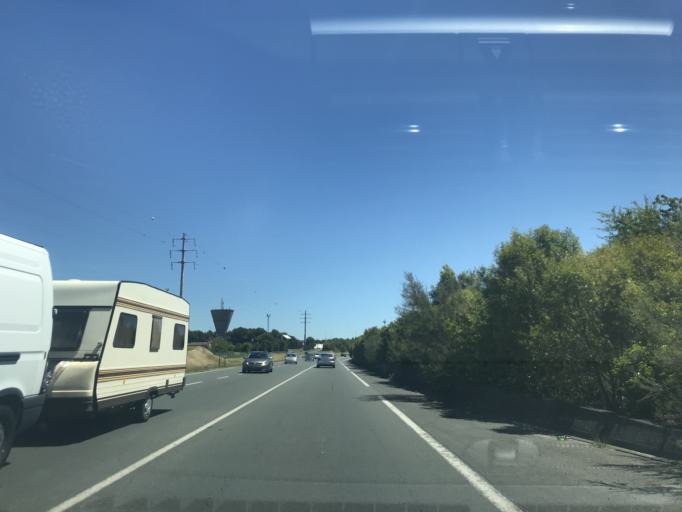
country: FR
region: Poitou-Charentes
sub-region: Departement de la Charente-Maritime
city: Royan
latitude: 45.6293
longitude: -1.0040
